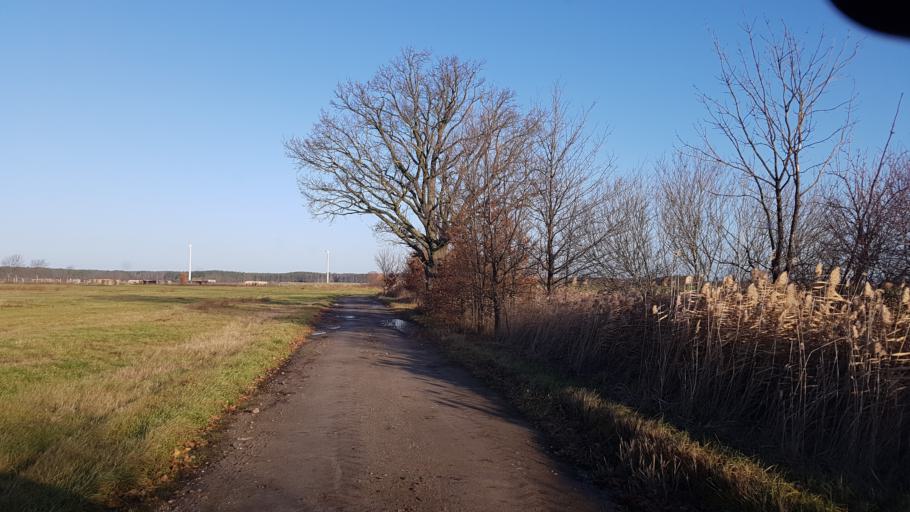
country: DE
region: Brandenburg
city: Schonborn
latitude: 51.5864
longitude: 13.5166
